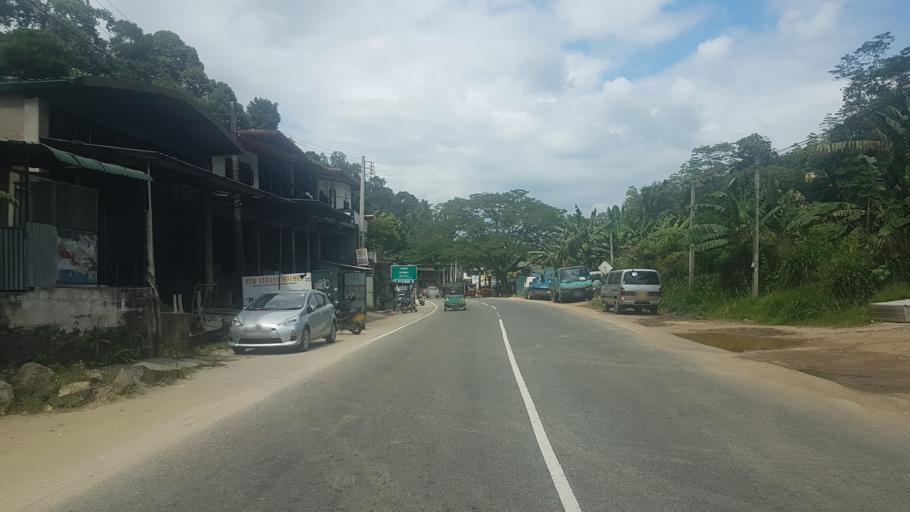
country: LK
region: Central
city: Gampola
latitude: 7.2095
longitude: 80.5987
